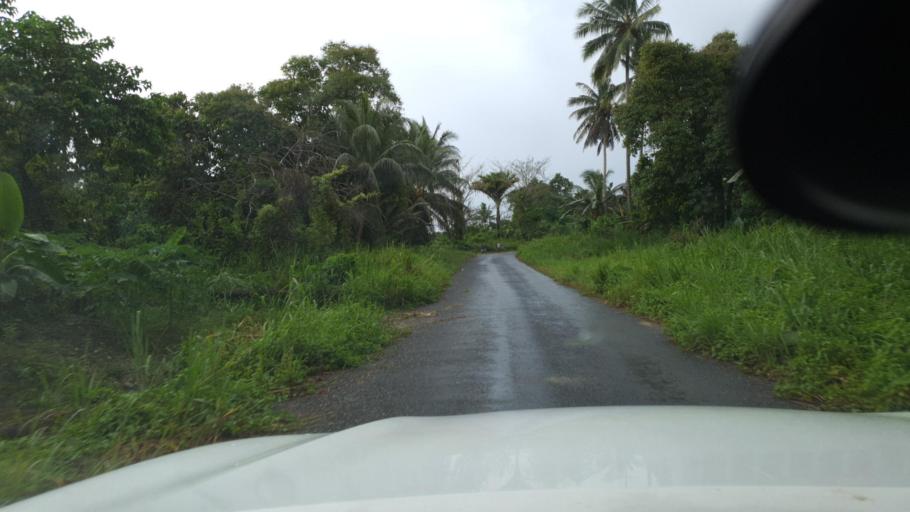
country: SB
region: Guadalcanal
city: Honiara
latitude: -9.4674
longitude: 160.3595
